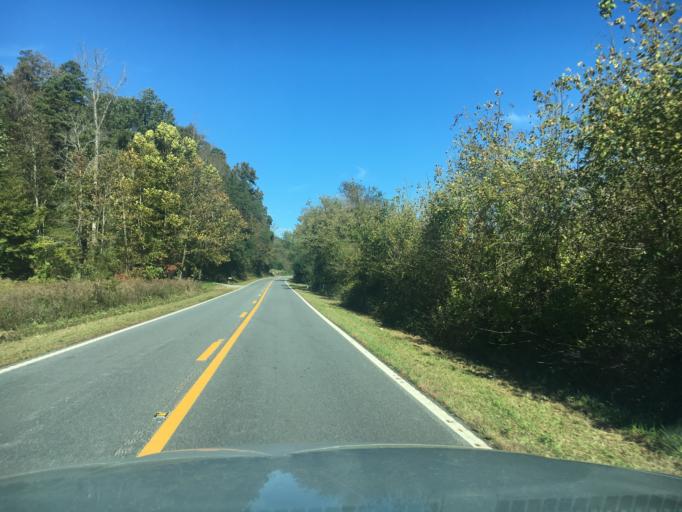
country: US
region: North Carolina
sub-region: Rutherford County
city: Spindale
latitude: 35.5267
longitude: -81.8557
